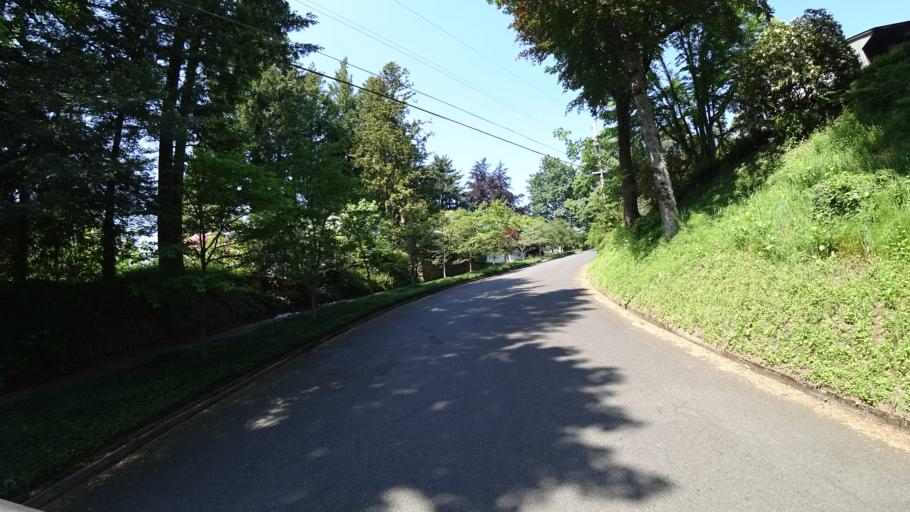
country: US
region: Oregon
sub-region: Multnomah County
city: Portland
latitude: 45.4931
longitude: -122.7025
